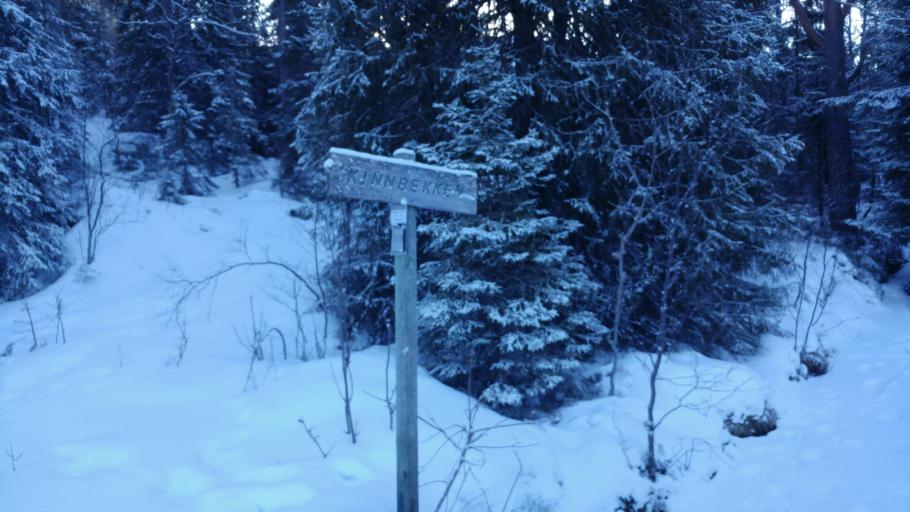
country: NO
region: Sor-Trondelag
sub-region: Trondheim
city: Trondheim
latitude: 63.4400
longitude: 10.3099
